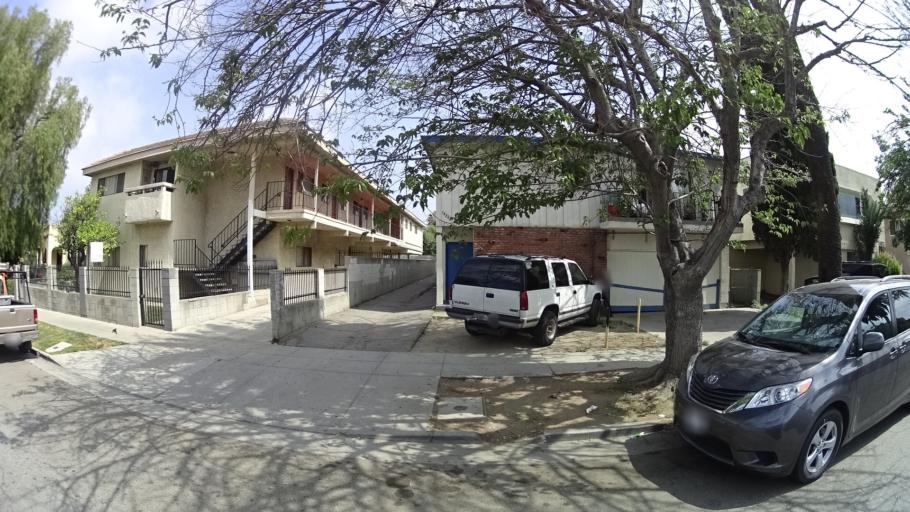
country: US
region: California
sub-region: Los Angeles County
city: Van Nuys
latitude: 34.1857
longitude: -118.4564
